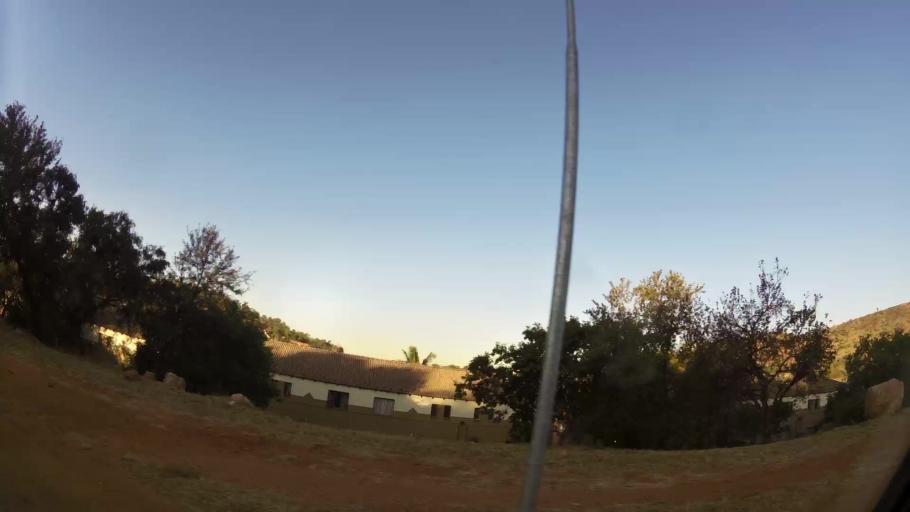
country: ZA
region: North-West
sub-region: Bojanala Platinum District Municipality
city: Rustenburg
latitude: -25.7133
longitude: 27.2402
